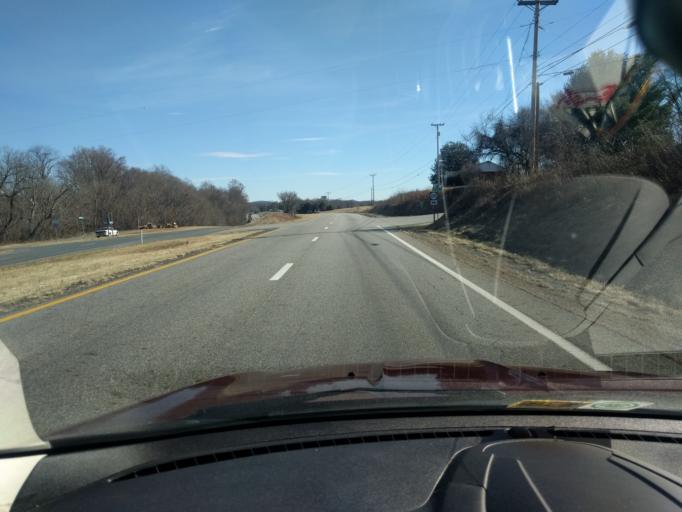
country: US
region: Virginia
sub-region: Botetourt County
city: Blue Ridge
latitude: 37.3581
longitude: -79.6721
